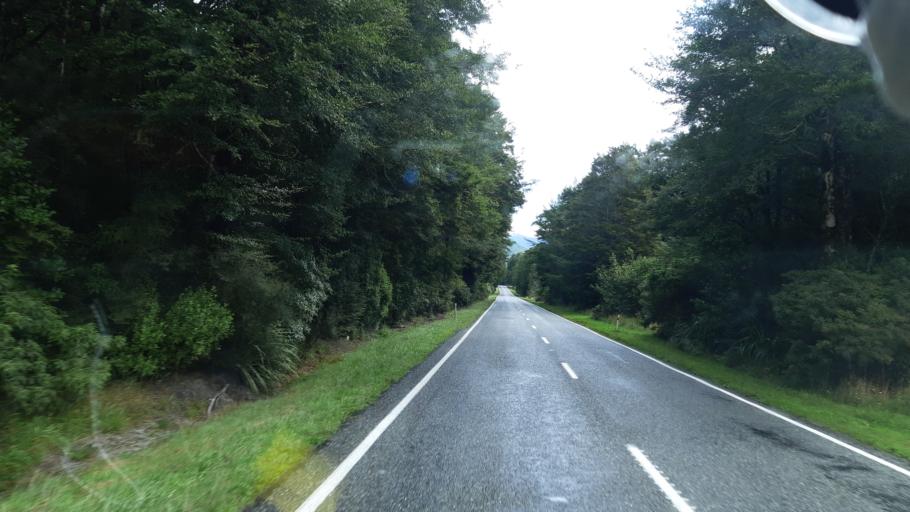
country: NZ
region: Canterbury
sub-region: Hurunui District
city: Amberley
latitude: -42.3806
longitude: 172.3197
